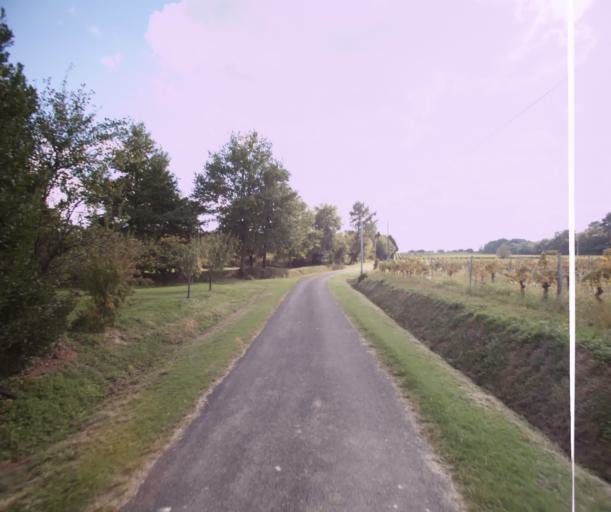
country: FR
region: Midi-Pyrenees
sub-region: Departement du Gers
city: Cazaubon
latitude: 43.8953
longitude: -0.0442
